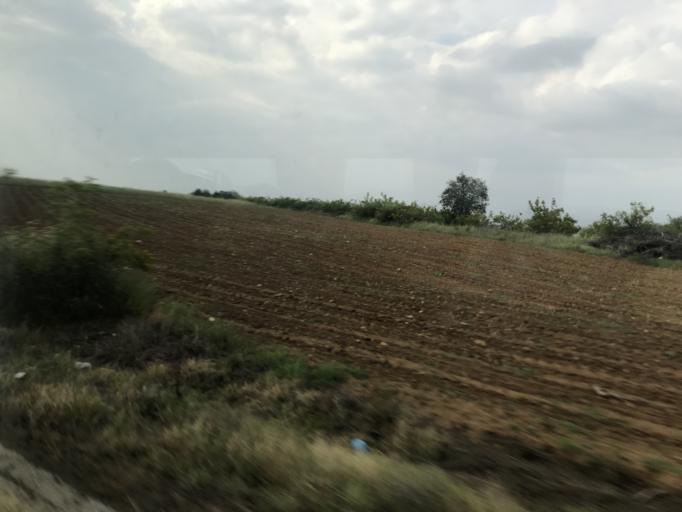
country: GR
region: East Macedonia and Thrace
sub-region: Nomos Rodopis
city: Sapes
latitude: 41.0329
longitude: 25.6781
